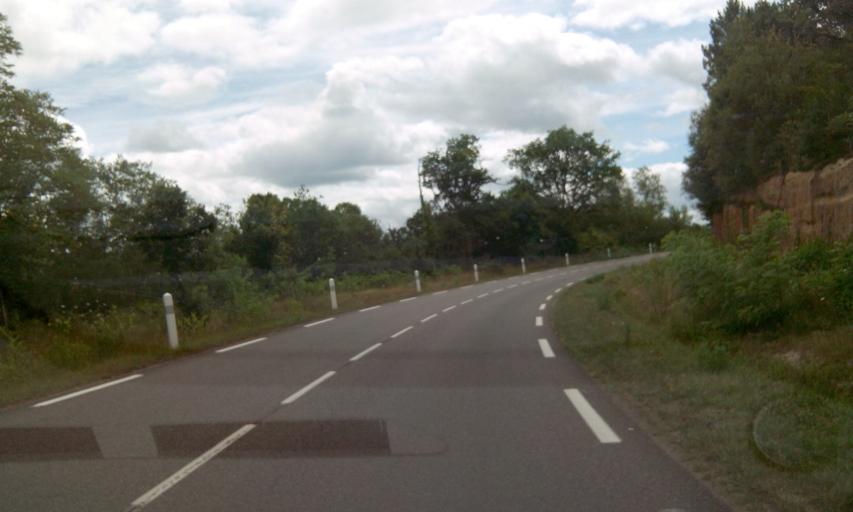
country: FR
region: Limousin
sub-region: Departement de la Correze
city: Brive-la-Gaillarde
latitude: 45.1312
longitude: 1.5539
